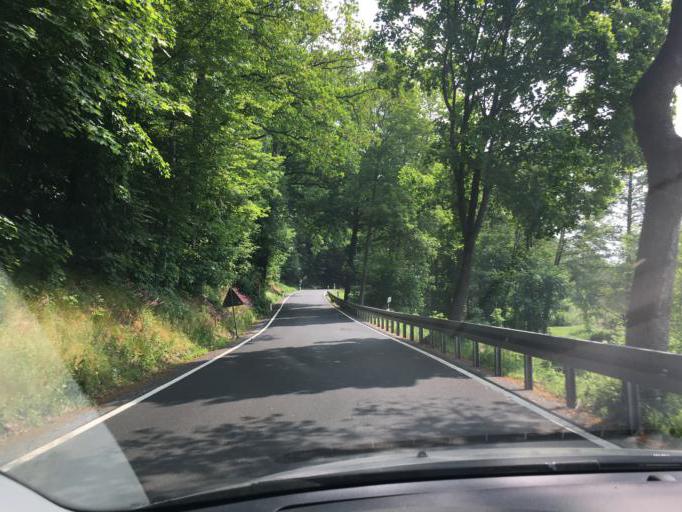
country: DE
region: Saxony
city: Colditz
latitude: 51.1223
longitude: 12.8061
